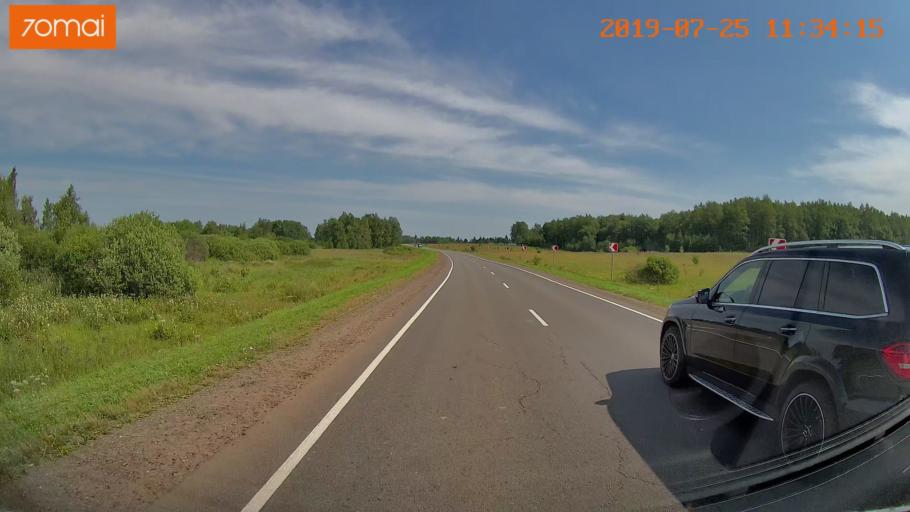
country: RU
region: Ivanovo
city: Privolzhsk
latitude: 57.3979
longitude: 41.4090
